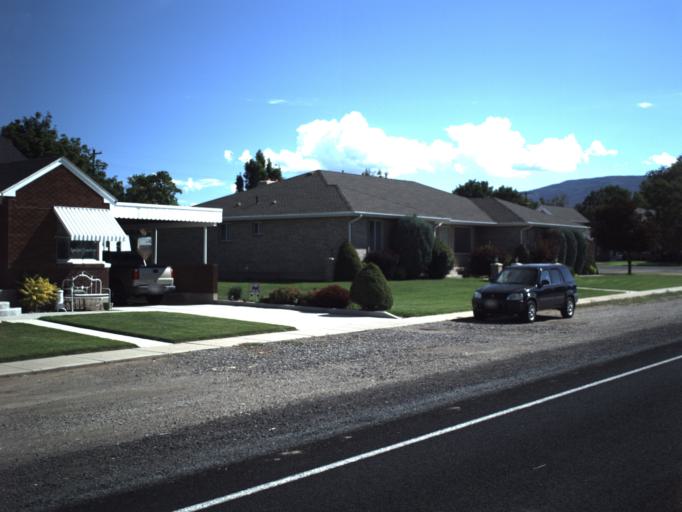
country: US
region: Utah
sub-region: Beaver County
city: Beaver
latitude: 38.2769
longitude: -112.6388
